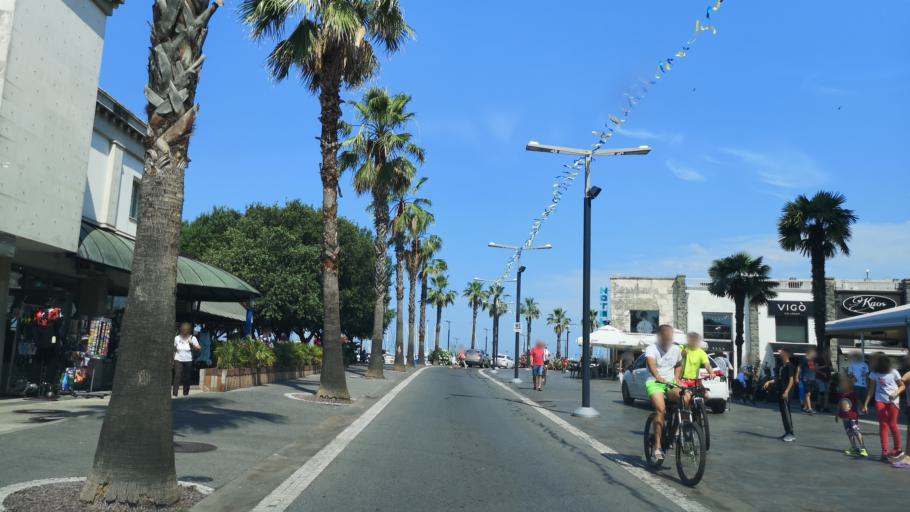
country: SI
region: Koper-Capodistria
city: Koper
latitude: 45.5465
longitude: 13.7262
